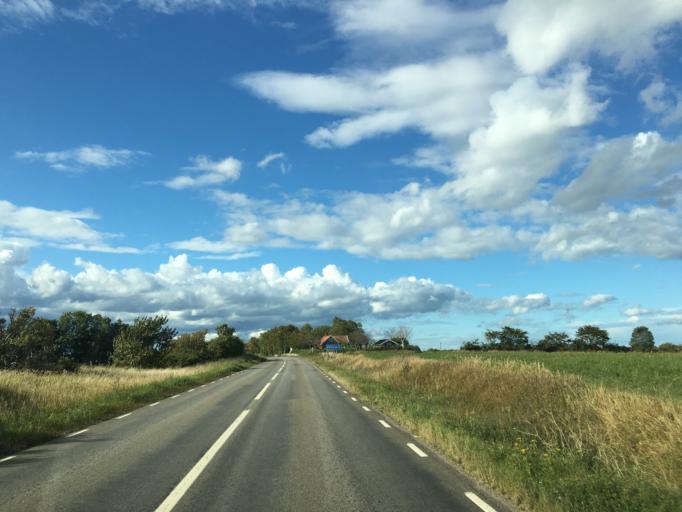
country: SE
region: Kalmar
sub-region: Morbylanga Kommun
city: Moerbylanga
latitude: 56.4773
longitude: 16.4296
